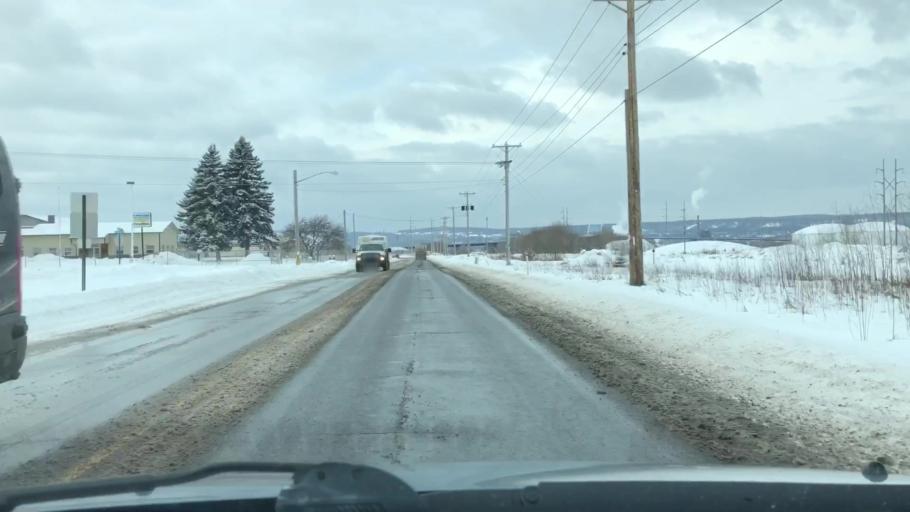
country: US
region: Wisconsin
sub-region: Douglas County
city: Superior
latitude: 46.7280
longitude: -92.1198
